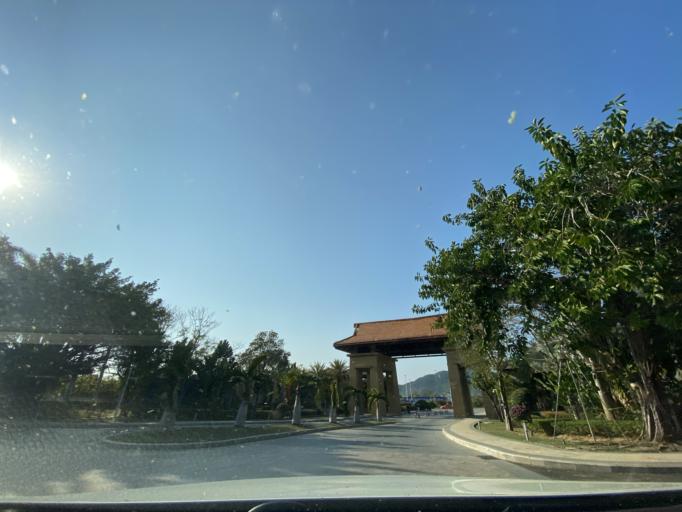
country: CN
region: Hainan
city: Haitangwan
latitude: 18.4034
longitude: 109.7799
